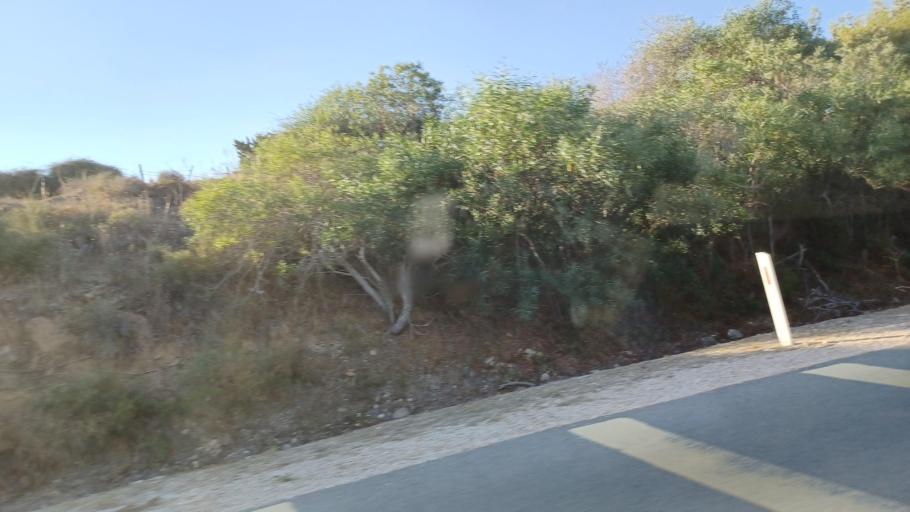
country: CY
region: Larnaka
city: Xylotymbou
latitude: 34.9841
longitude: 33.7410
